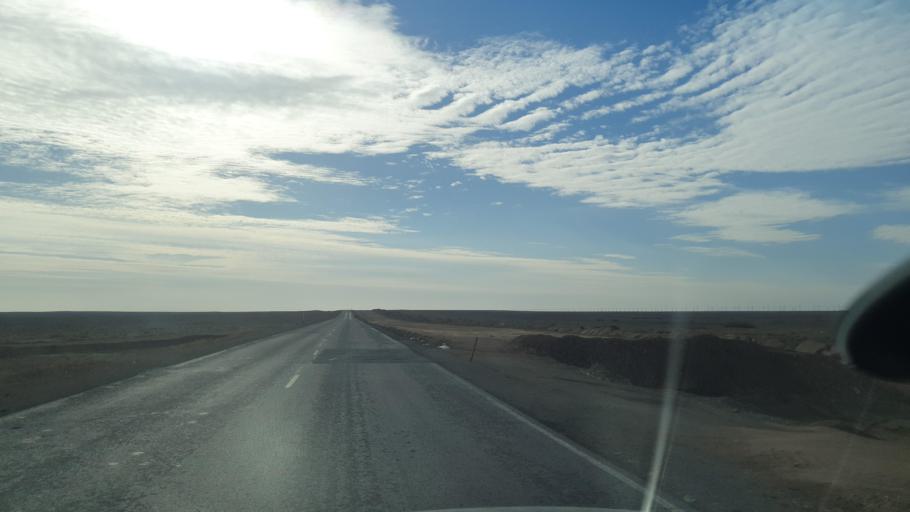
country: KZ
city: Priozersk
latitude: 45.9594
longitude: 73.5424
